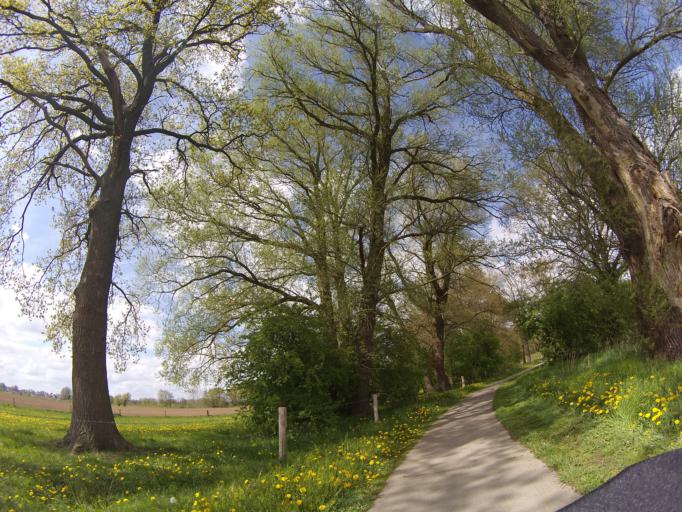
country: NL
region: Overijssel
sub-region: Gemeente Dalfsen
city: Dalfsen
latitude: 52.5039
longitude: 6.2739
